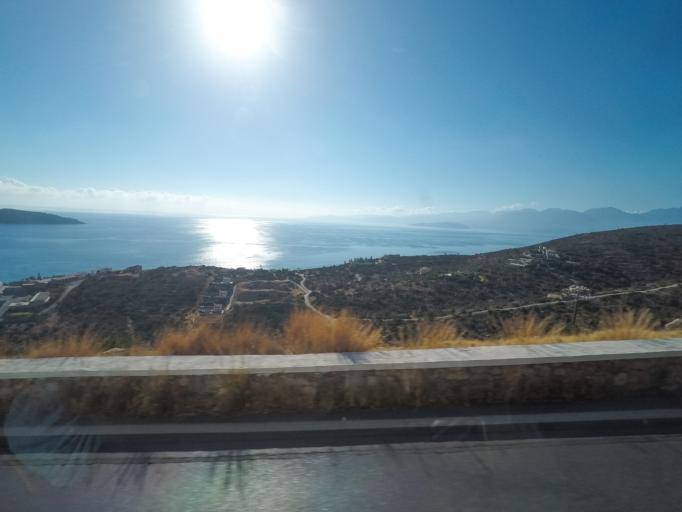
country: GR
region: Crete
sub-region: Nomos Lasithiou
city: Skhisma
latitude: 35.2365
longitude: 25.7284
